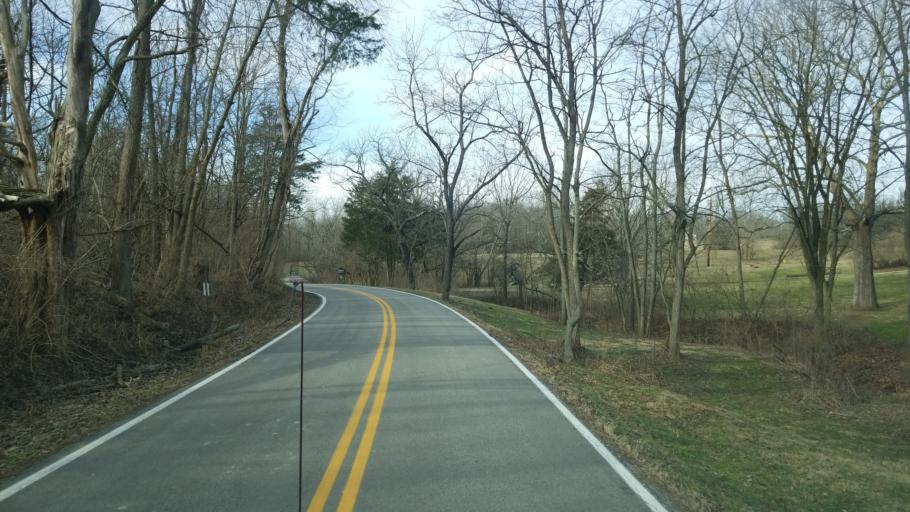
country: US
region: Ohio
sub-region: Warren County
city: Waynesville
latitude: 39.4522
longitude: -84.0869
